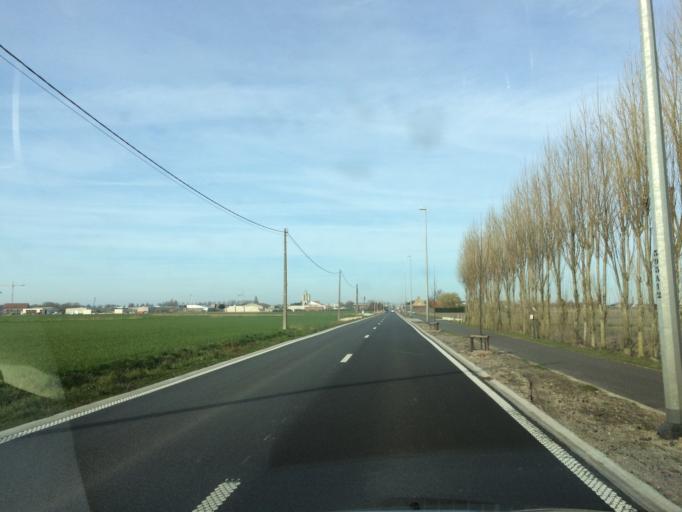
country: BE
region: Flanders
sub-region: Provincie West-Vlaanderen
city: Nieuwpoort
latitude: 51.1195
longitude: 2.7654
